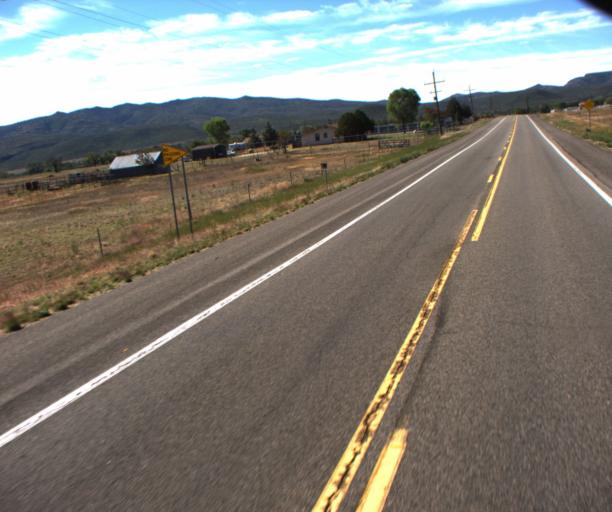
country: US
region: Arizona
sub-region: Yavapai County
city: Congress
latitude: 34.2835
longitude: -112.7228
